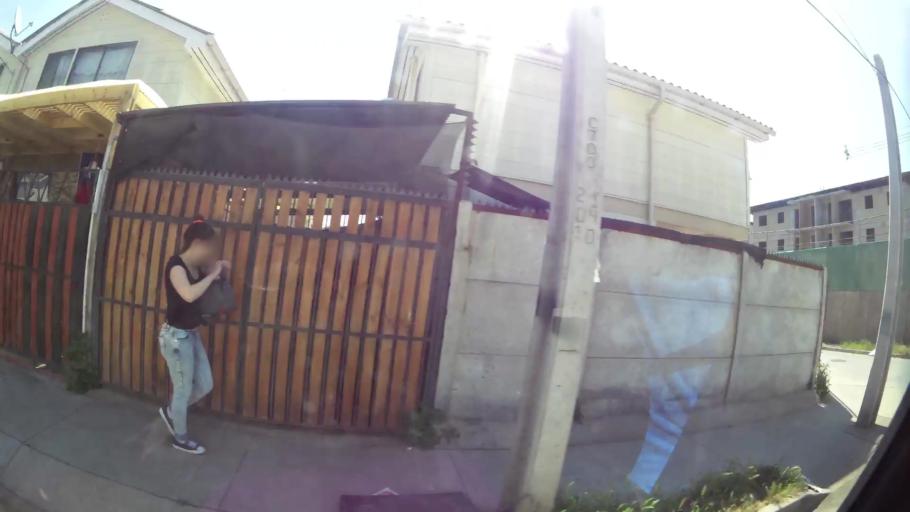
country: CL
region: Santiago Metropolitan
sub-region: Provincia de Talagante
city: Penaflor
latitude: -33.5750
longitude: -70.8025
